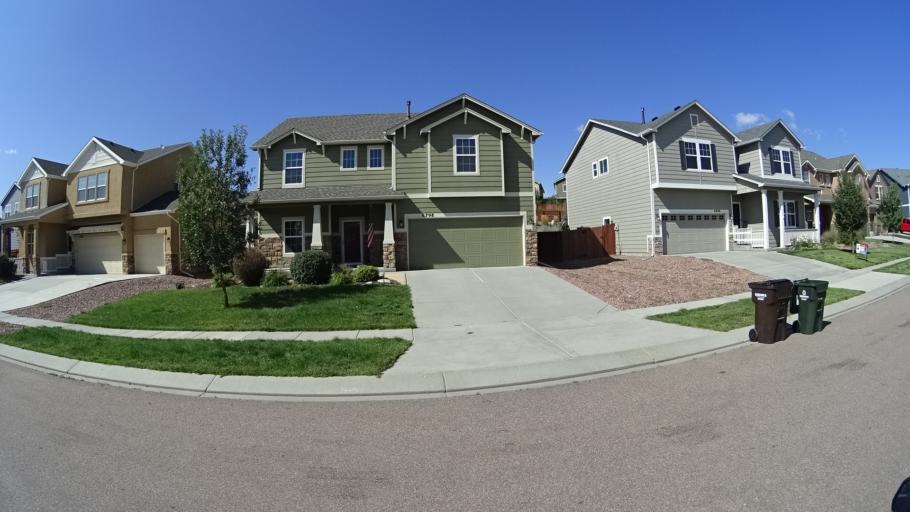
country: US
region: Colorado
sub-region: El Paso County
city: Cimarron Hills
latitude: 38.9288
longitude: -104.7076
